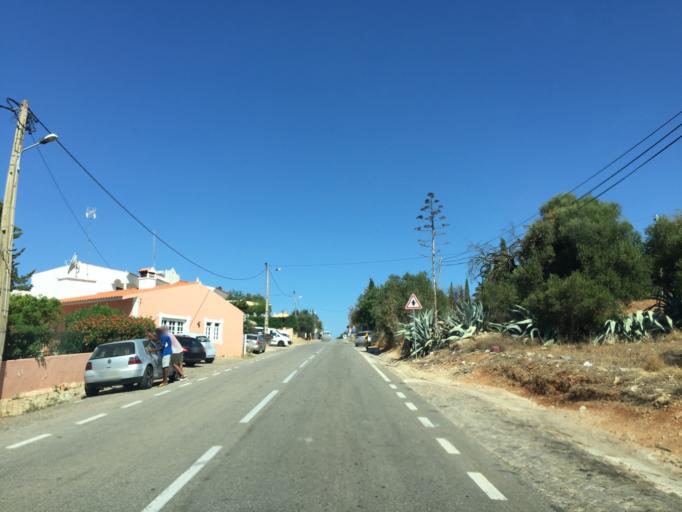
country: PT
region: Faro
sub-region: Loule
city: Vilamoura
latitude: 37.1162
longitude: -8.0927
